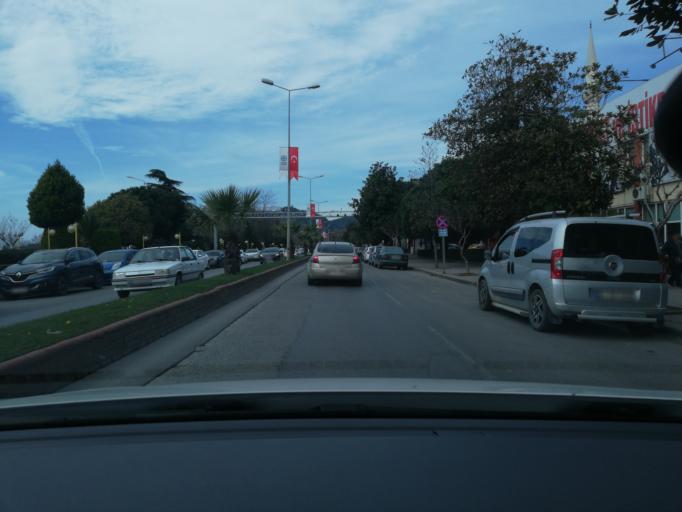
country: TR
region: Zonguldak
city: Eregli
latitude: 41.2827
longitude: 31.4153
